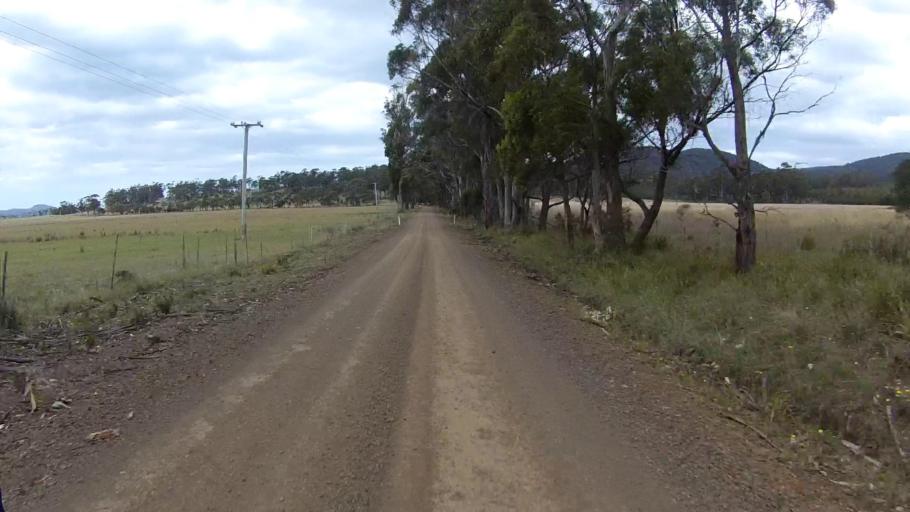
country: AU
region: Tasmania
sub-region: Sorell
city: Sorell
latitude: -42.6525
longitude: 147.9126
